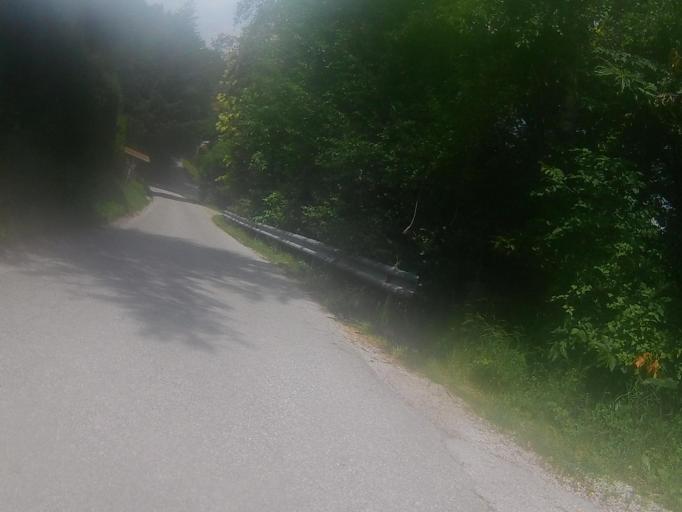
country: SI
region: Maribor
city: Kamnica
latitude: 46.5955
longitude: 15.6114
